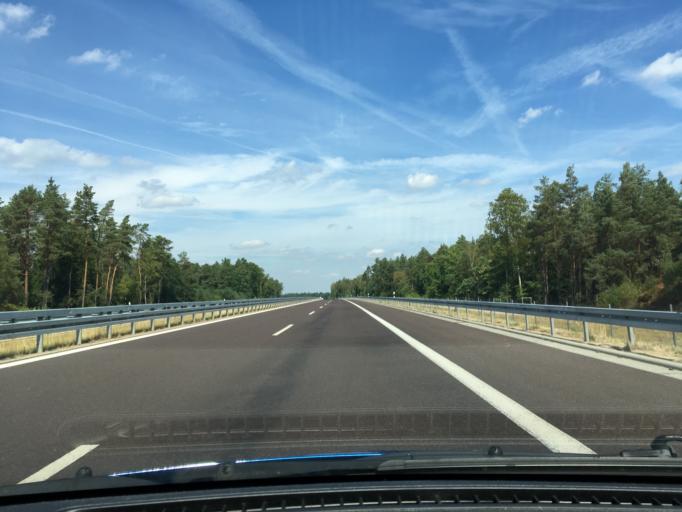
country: DE
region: Mecklenburg-Vorpommern
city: Ludwigslust
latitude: 53.3195
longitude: 11.5281
